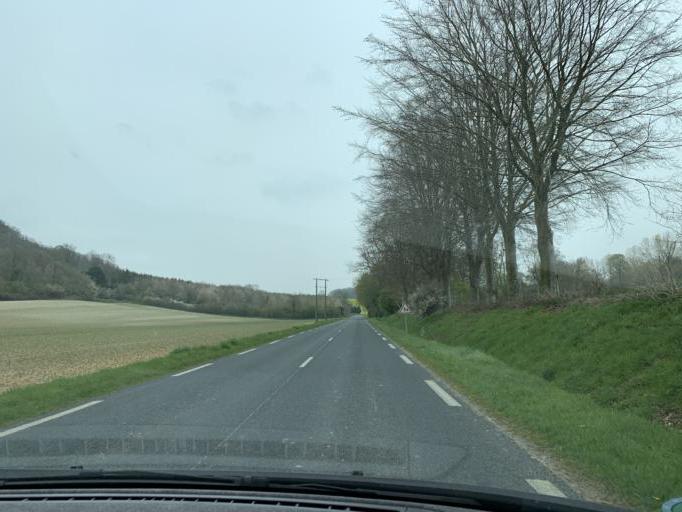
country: FR
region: Haute-Normandie
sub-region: Departement de la Seine-Maritime
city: Londinieres
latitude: 49.8407
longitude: 1.4423
